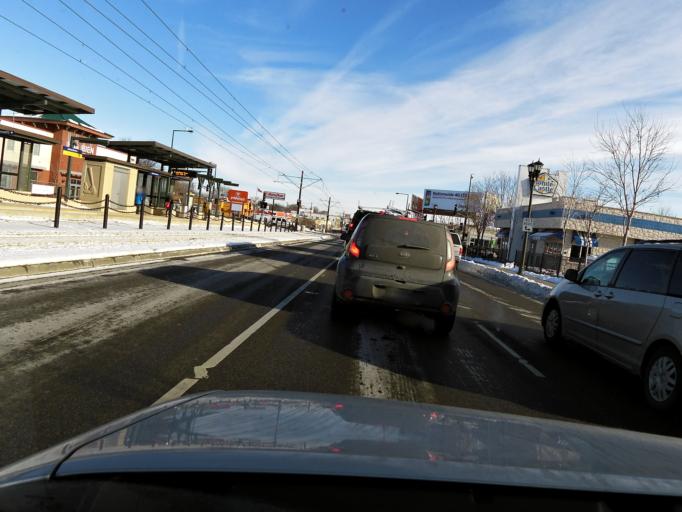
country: US
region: Minnesota
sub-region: Ramsey County
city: Falcon Heights
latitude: 44.9556
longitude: -93.1476
